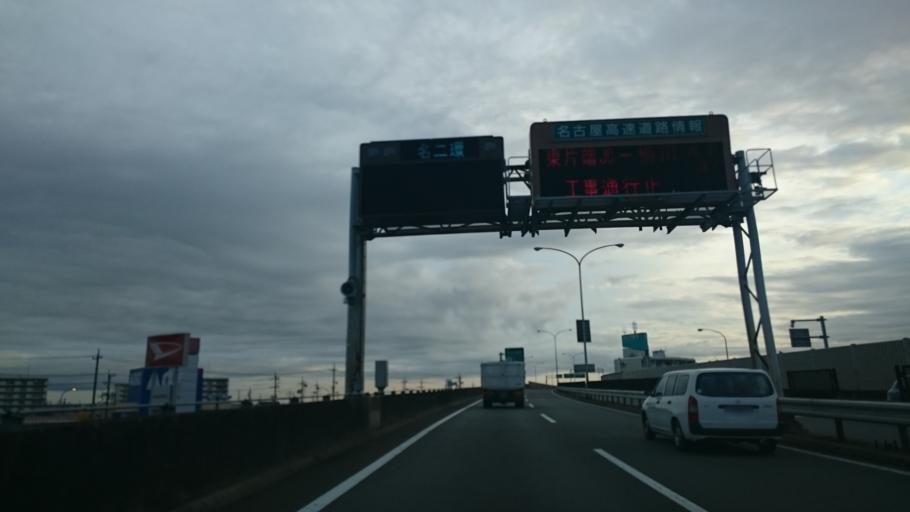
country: JP
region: Aichi
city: Kanie
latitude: 35.1554
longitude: 136.8077
